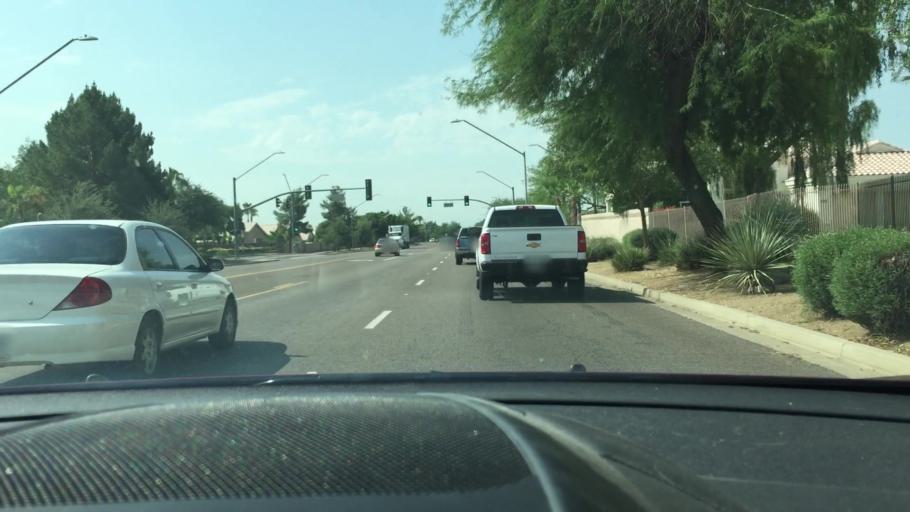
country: US
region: Arizona
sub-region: Maricopa County
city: Peoria
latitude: 33.6854
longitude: -112.2032
